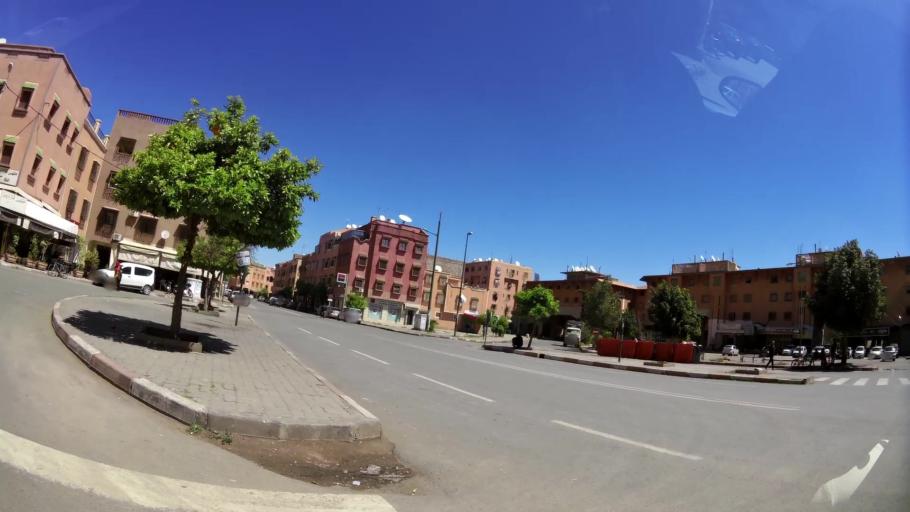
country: MA
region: Marrakech-Tensift-Al Haouz
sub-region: Marrakech
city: Marrakesh
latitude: 31.6342
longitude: -8.0678
